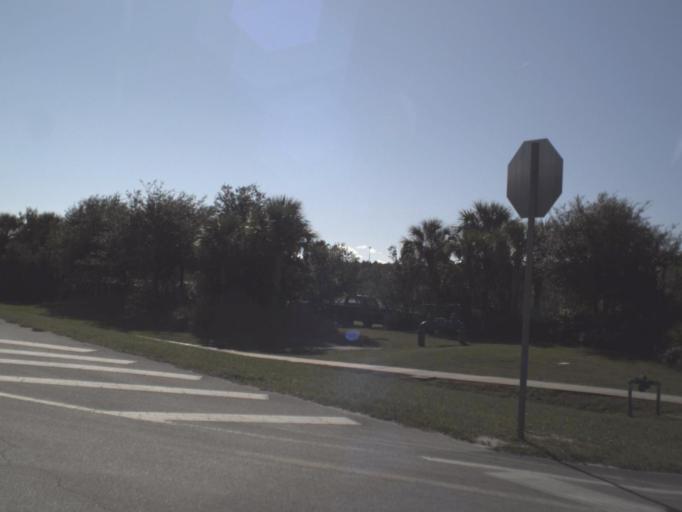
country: US
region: Florida
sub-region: Volusia County
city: Daytona Beach
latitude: 29.1673
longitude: -81.0783
